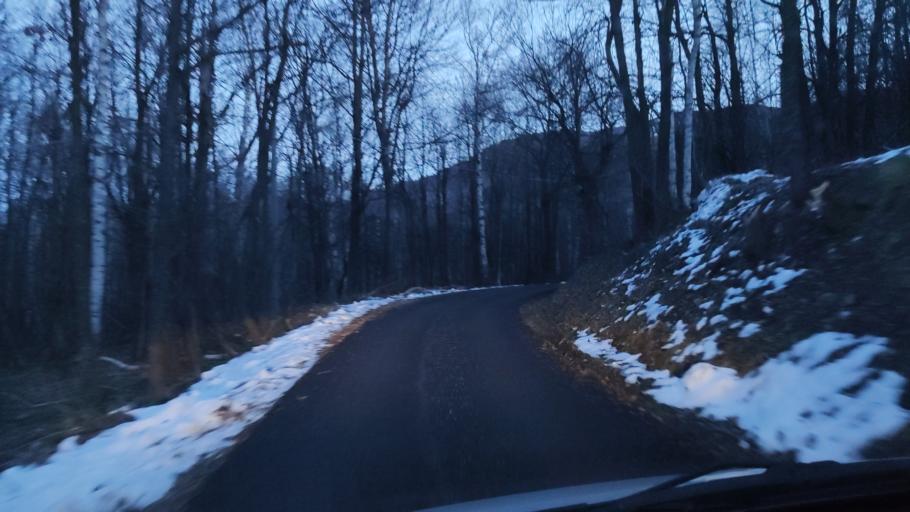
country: IT
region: Piedmont
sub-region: Provincia di Cuneo
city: Viola
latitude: 44.2780
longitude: 7.9636
